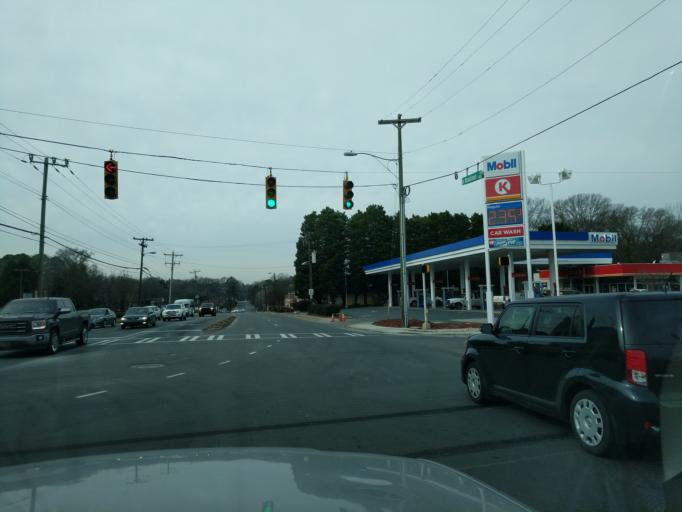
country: US
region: North Carolina
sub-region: Mecklenburg County
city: Charlotte
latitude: 35.1721
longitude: -80.8510
